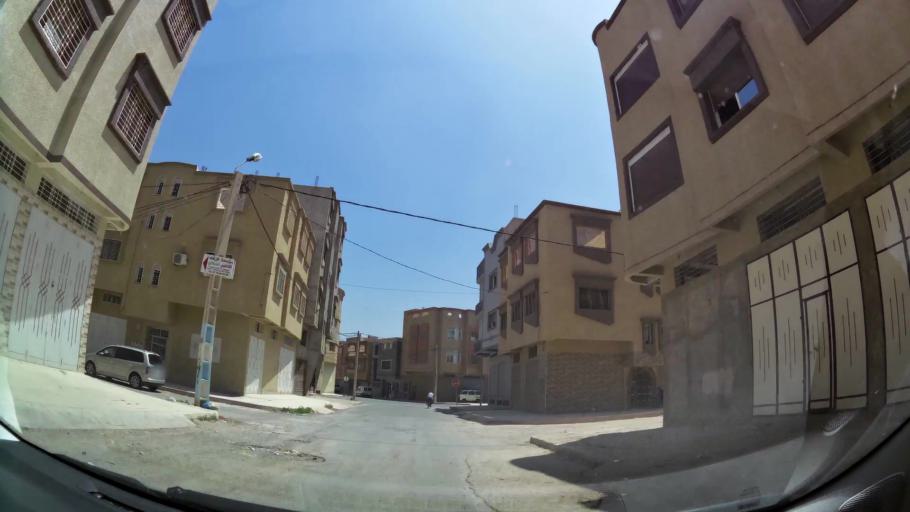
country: MA
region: Oriental
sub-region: Oujda-Angad
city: Oujda
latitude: 34.6963
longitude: -1.8973
